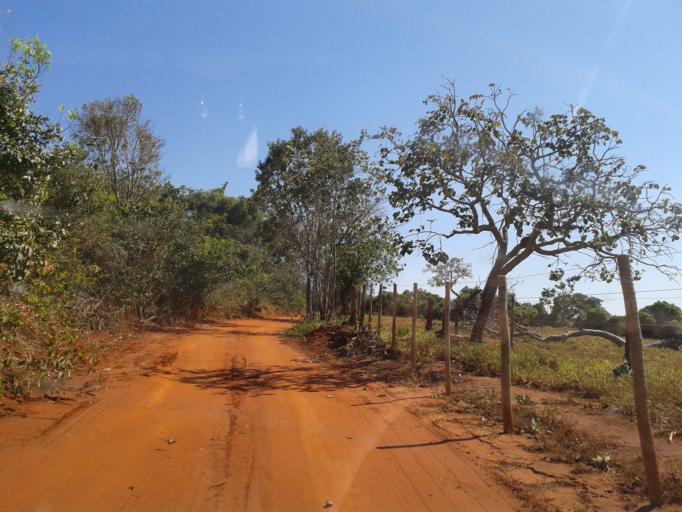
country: BR
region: Minas Gerais
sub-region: Monte Alegre De Minas
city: Monte Alegre de Minas
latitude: -18.8783
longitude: -49.1306
